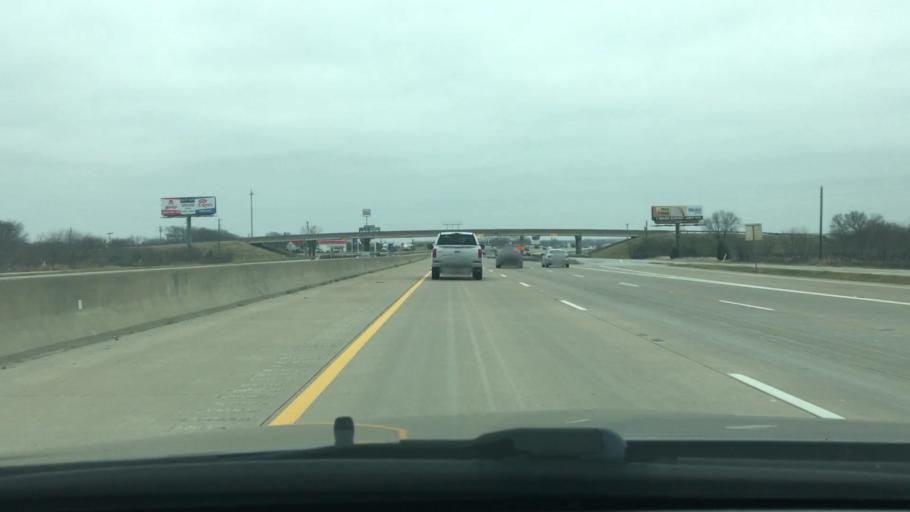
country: US
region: Texas
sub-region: Navarro County
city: Corsicana
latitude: 32.2020
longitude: -96.4751
